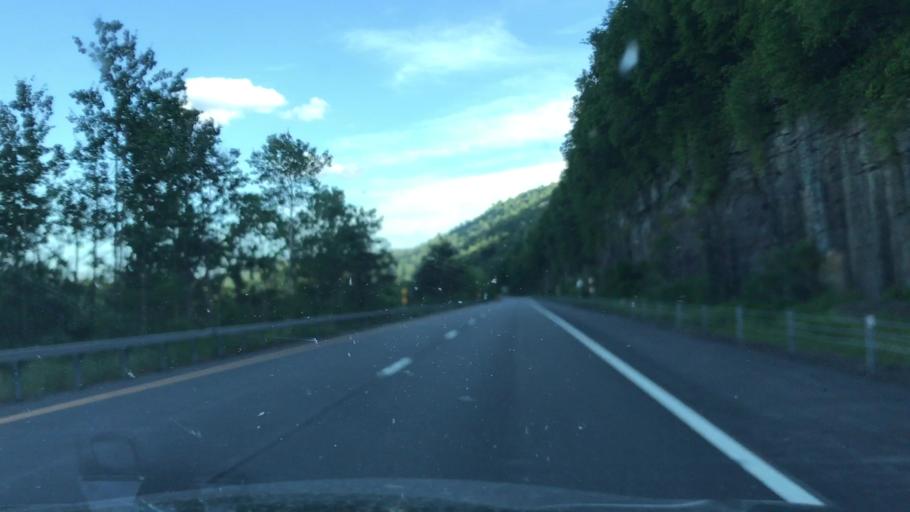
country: US
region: New York
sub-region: Sullivan County
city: Livingston Manor
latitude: 41.9496
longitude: -74.9325
